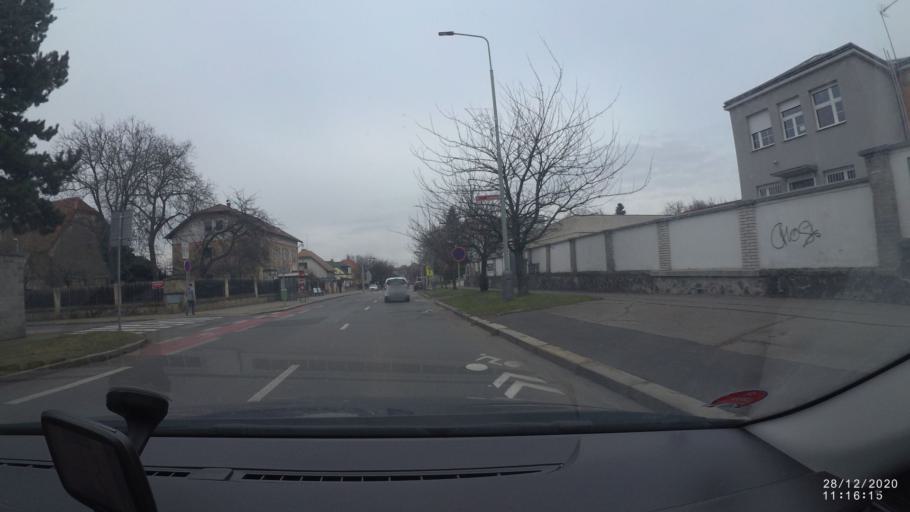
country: CZ
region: Praha
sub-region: Praha 18
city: Letnany
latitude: 50.1345
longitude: 14.5139
